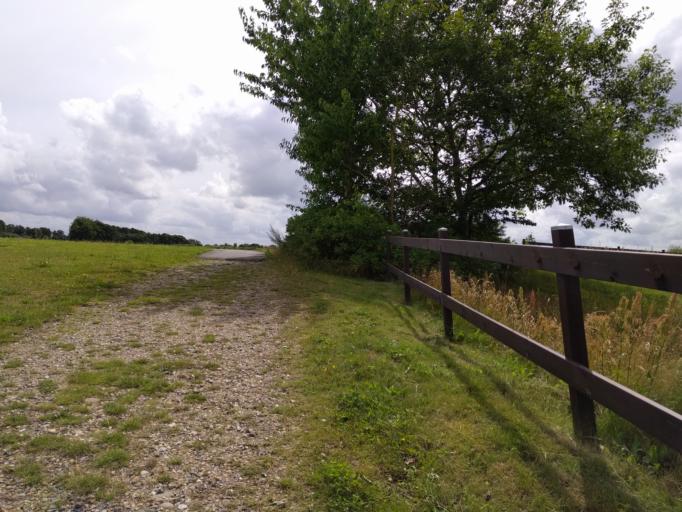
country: DK
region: Central Jutland
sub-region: Skanderborg Kommune
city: Ry
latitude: 56.0795
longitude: 9.7796
